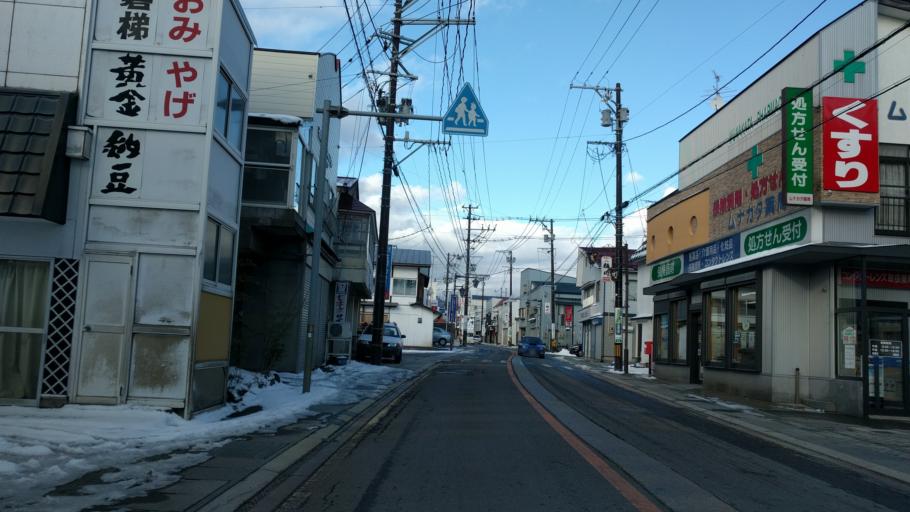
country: JP
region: Fukushima
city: Inawashiro
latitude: 37.5595
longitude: 140.1069
